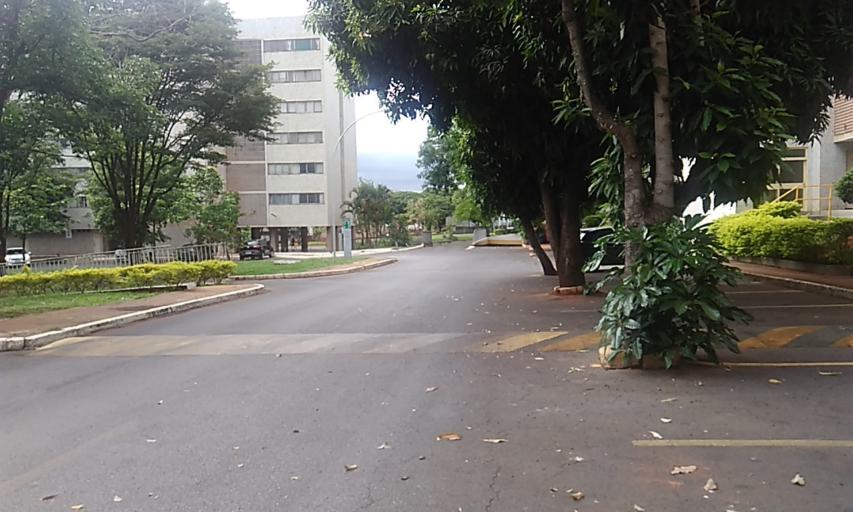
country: BR
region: Federal District
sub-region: Brasilia
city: Brasilia
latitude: -15.7794
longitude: -47.8837
